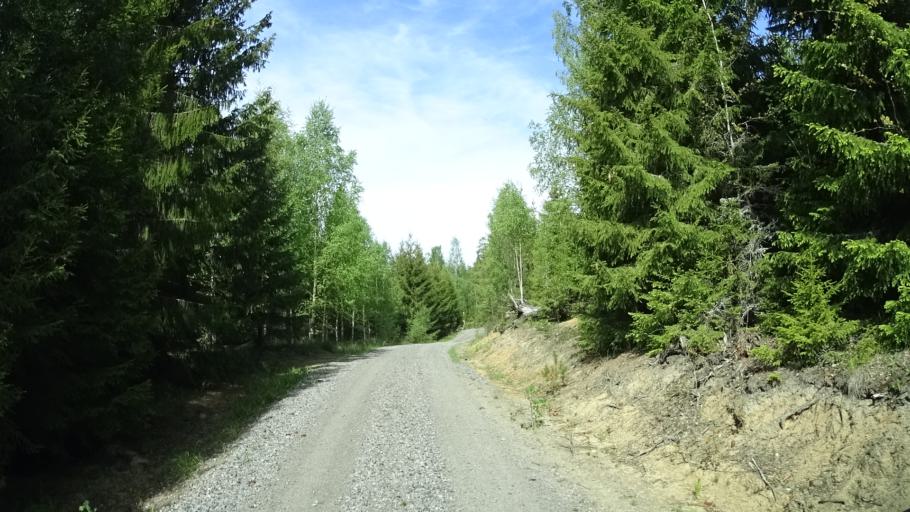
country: SE
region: OEstergoetland
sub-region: Finspangs Kommun
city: Finspang
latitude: 58.7957
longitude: 15.8532
